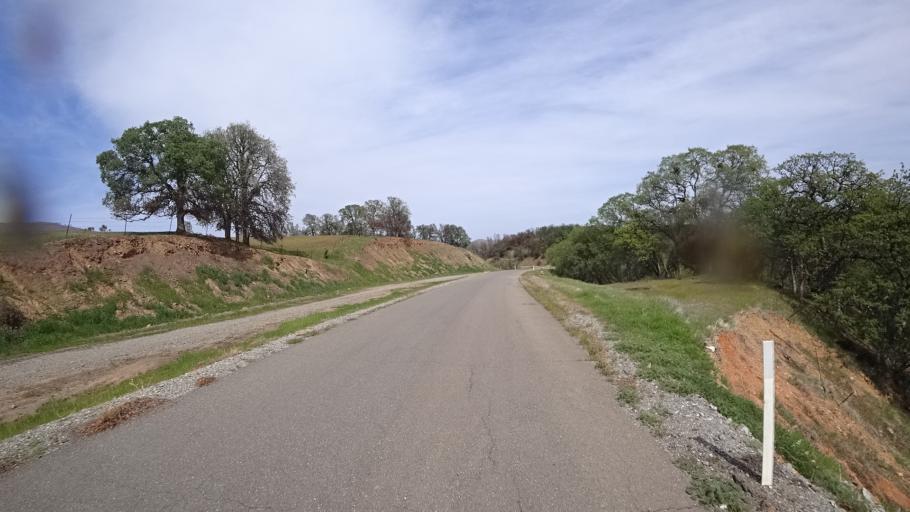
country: US
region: California
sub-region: Glenn County
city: Willows
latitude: 39.5794
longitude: -122.5992
